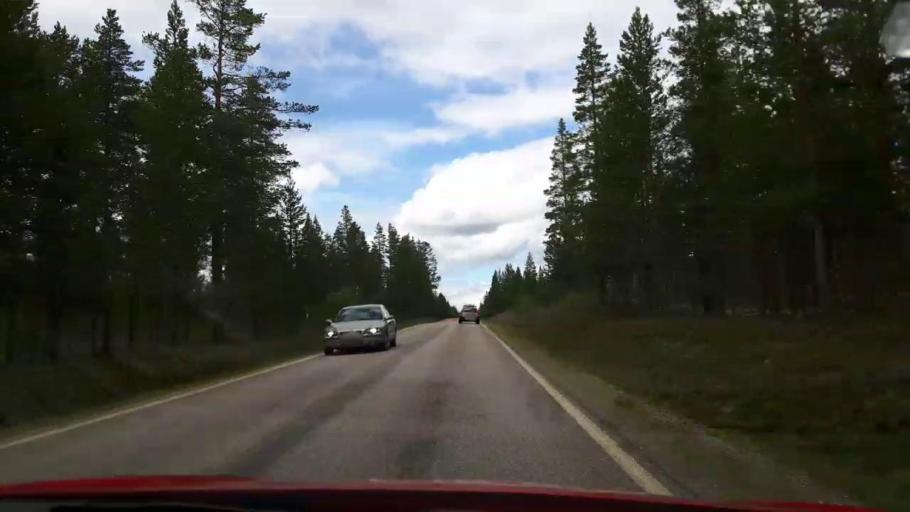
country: NO
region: Hedmark
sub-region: Trysil
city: Innbygda
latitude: 61.8430
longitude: 12.9555
